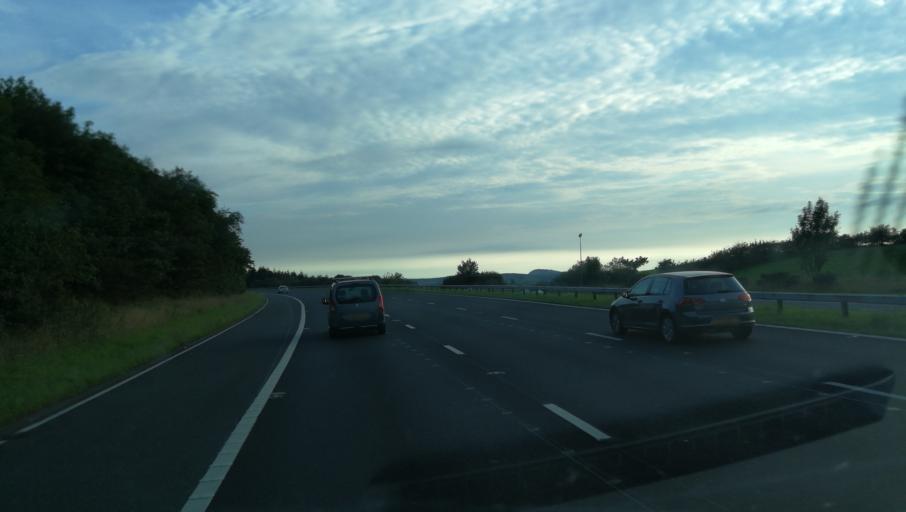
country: GB
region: England
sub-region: Cumbria
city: Kendal
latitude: 54.2682
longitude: -2.6822
